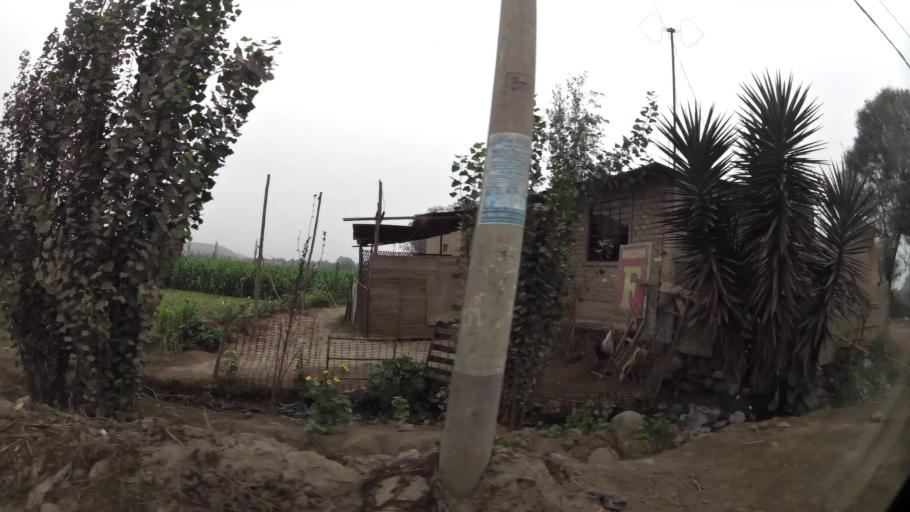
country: PE
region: Lima
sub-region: Lima
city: Carabayllo
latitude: -11.8576
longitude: -77.0188
